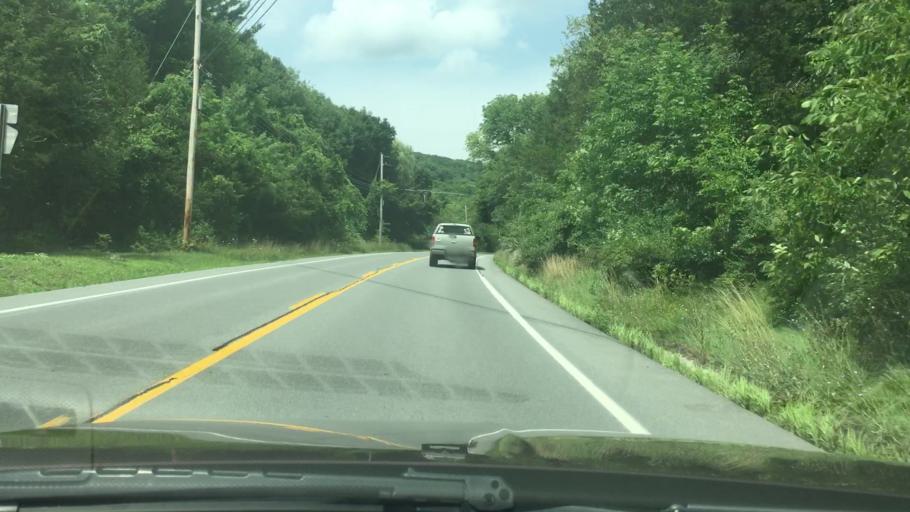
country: US
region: New York
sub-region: Dutchess County
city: Hillside Lake
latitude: 41.6302
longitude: -73.7023
